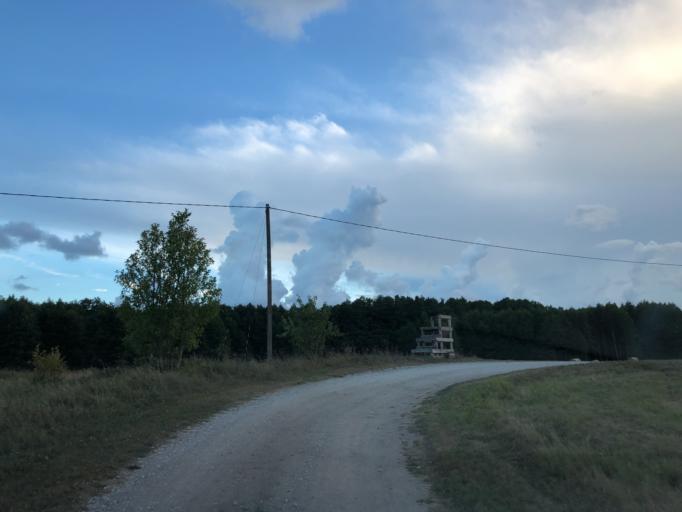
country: EE
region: Laeaene
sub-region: Haapsalu linn
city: Haapsalu
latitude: 58.7818
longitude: 23.4814
